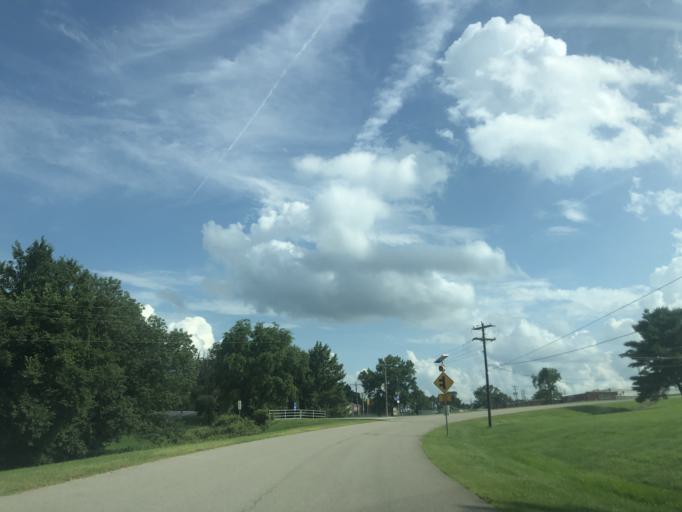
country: US
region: Tennessee
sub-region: Davidson County
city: Lakewood
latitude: 36.1652
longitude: -86.6387
